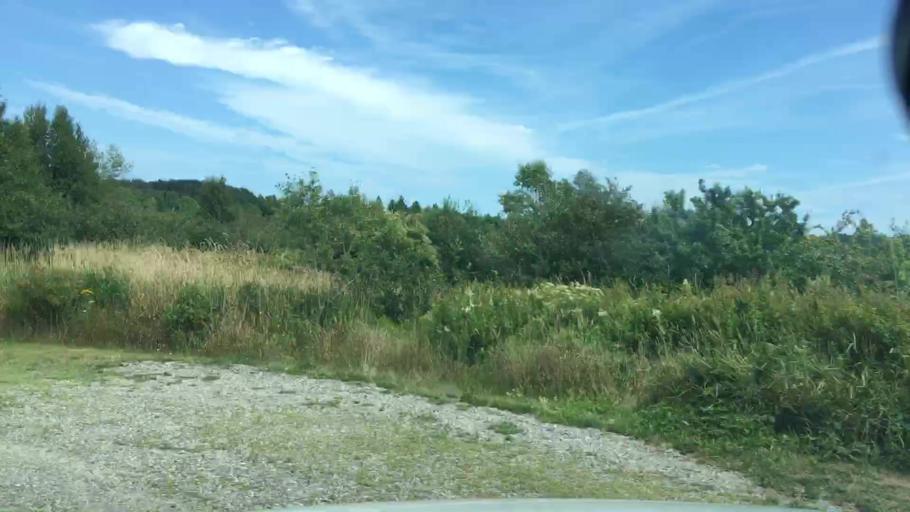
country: US
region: Maine
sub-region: Washington County
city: Eastport
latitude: 44.9054
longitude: -67.0126
